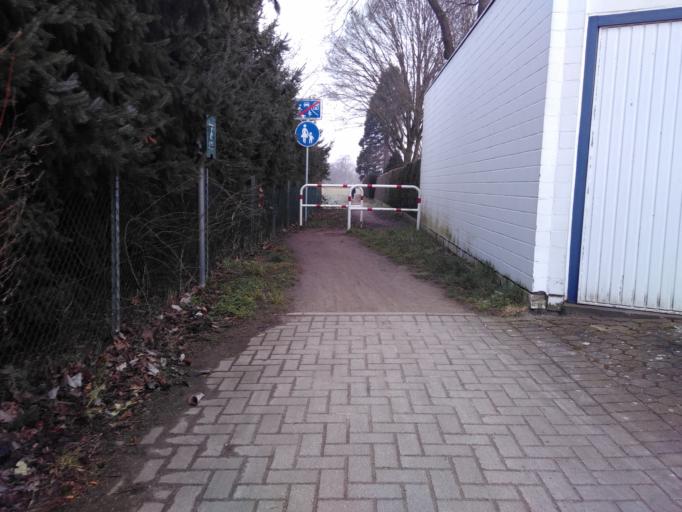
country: DE
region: North Rhine-Westphalia
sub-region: Regierungsbezirk Detmold
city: Verl
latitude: 51.8851
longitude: 8.4921
